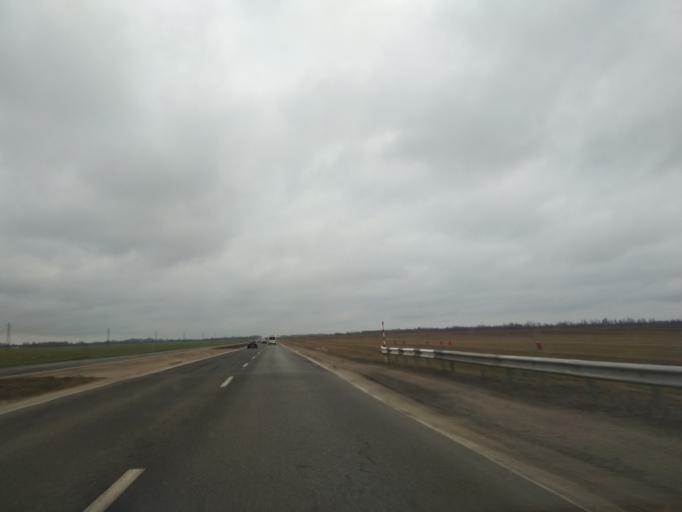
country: BY
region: Minsk
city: Dukora
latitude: 53.6568
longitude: 27.9561
